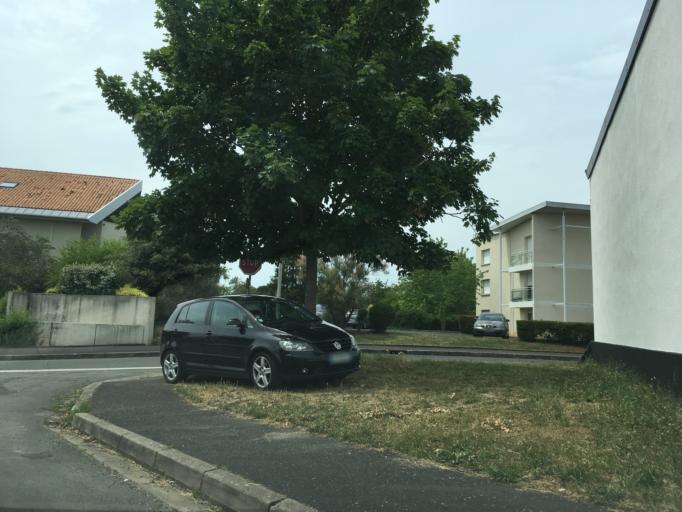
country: FR
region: Poitou-Charentes
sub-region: Departement des Deux-Sevres
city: Niort
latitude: 46.3207
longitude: -0.4756
